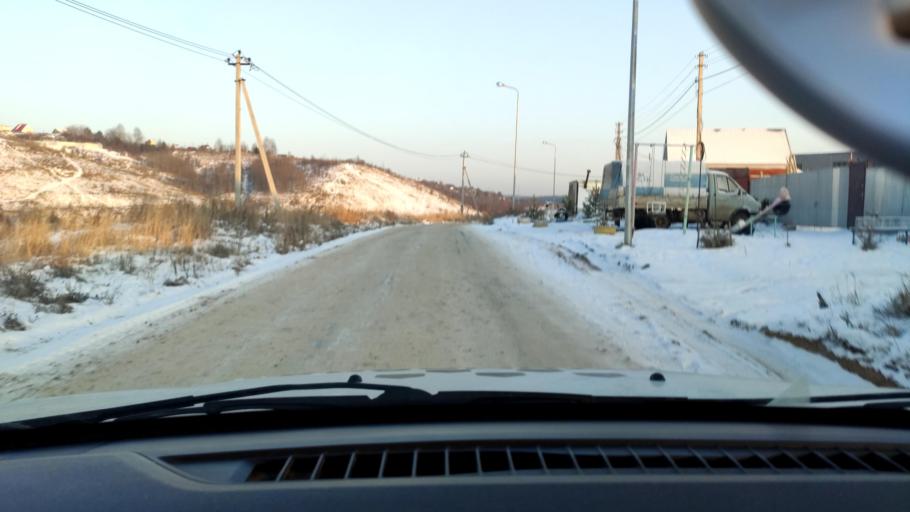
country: RU
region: Perm
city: Perm
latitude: 58.0283
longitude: 56.3475
